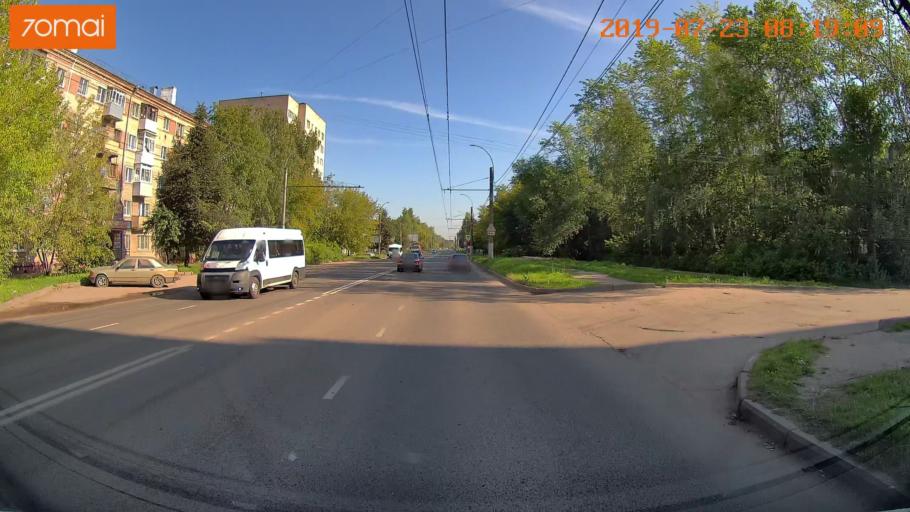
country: RU
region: Ivanovo
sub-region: Gorod Ivanovo
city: Ivanovo
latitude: 56.9665
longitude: 40.9626
